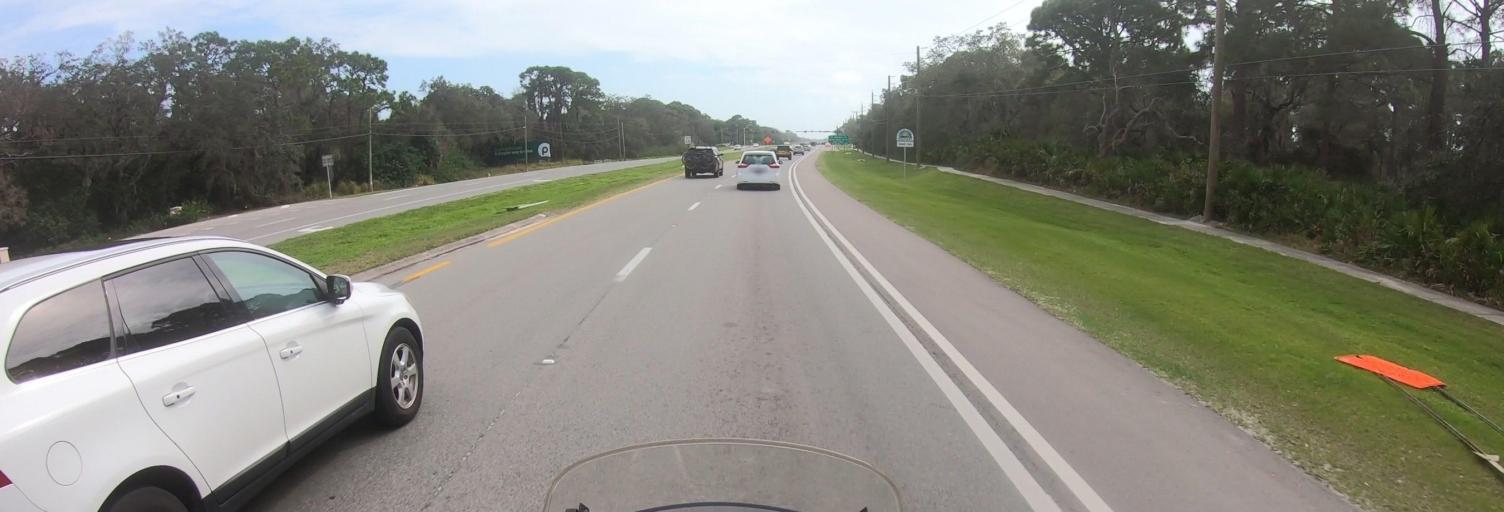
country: US
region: Florida
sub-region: Sarasota County
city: Vamo
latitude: 27.2186
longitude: -82.4919
